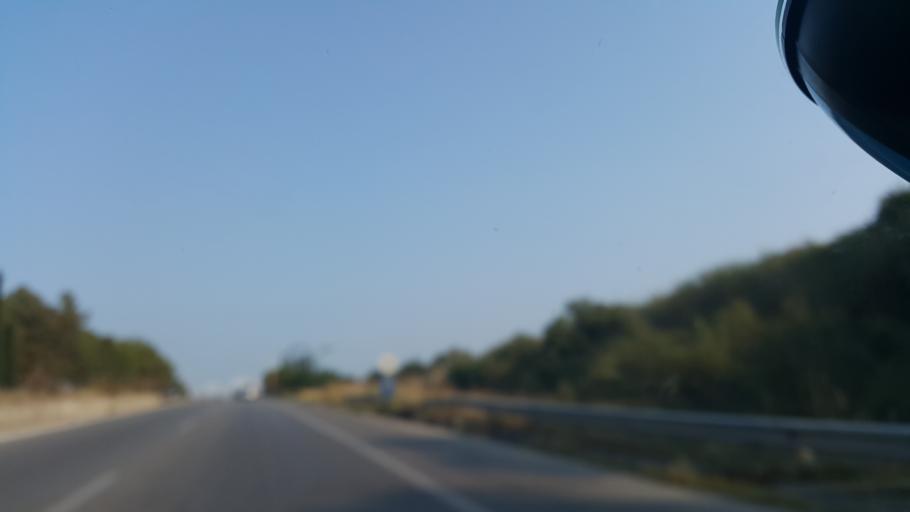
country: GR
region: Central Macedonia
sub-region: Nomos Thessalonikis
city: Kardia
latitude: 40.4542
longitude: 23.0065
